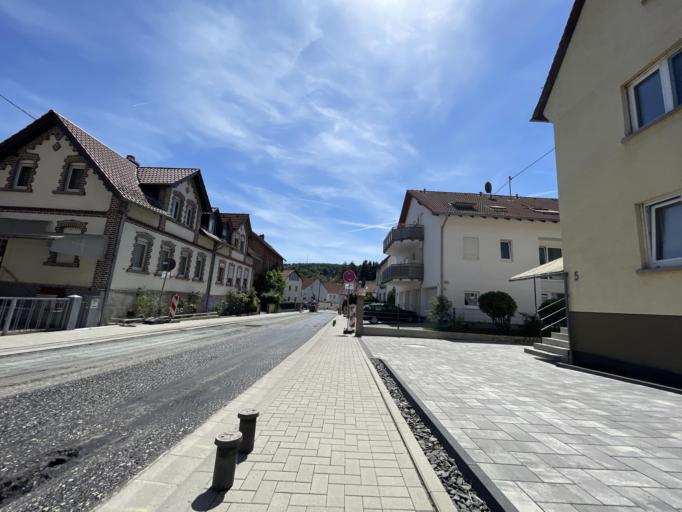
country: GB
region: England
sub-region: East Sussex
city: Eastbourne
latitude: 50.5901
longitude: 0.4551
